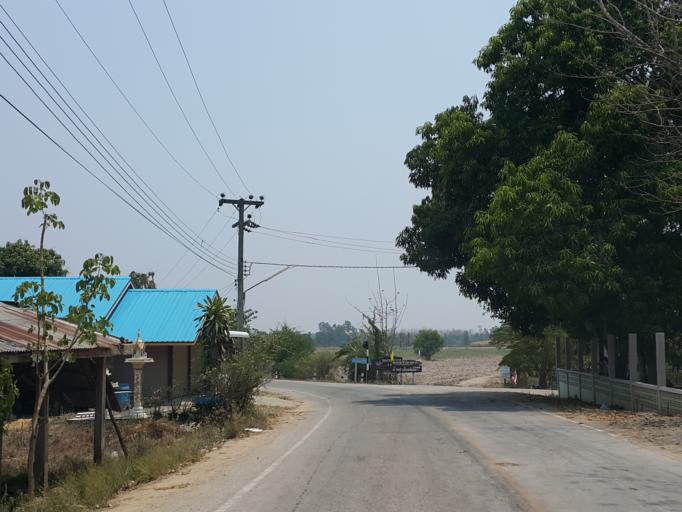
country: TH
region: Kamphaeng Phet
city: Pang Sila Thong
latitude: 15.9959
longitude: 99.3696
